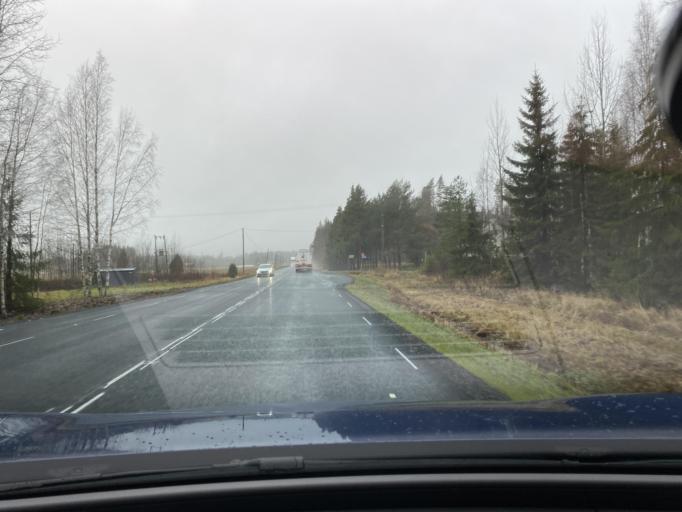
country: FI
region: Haeme
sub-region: Forssa
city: Ypaejae
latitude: 60.7756
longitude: 23.3322
